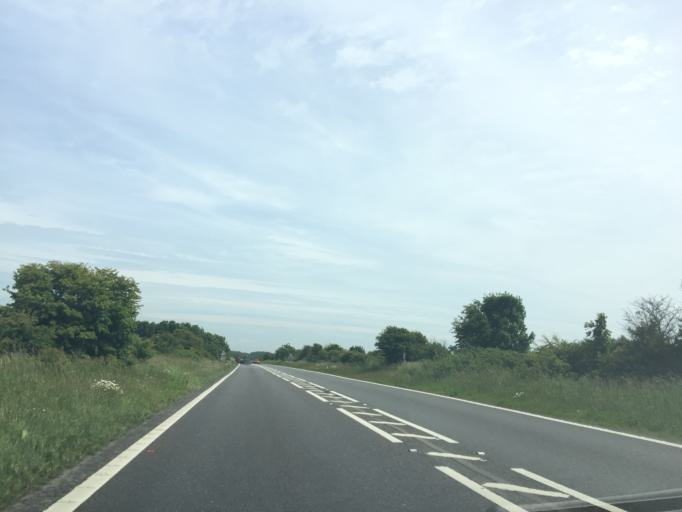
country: GB
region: England
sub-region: Kent
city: Dover
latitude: 51.1619
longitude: 1.2671
